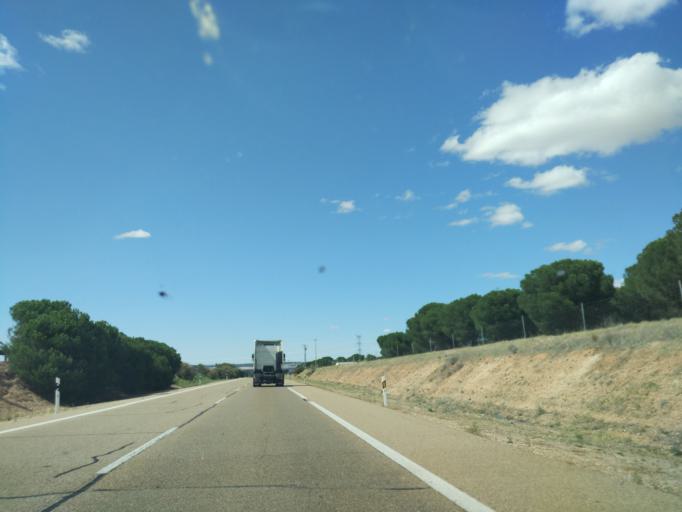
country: ES
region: Castille and Leon
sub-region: Provincia de Valladolid
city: Tordesillas
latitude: 41.4600
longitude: -4.9837
